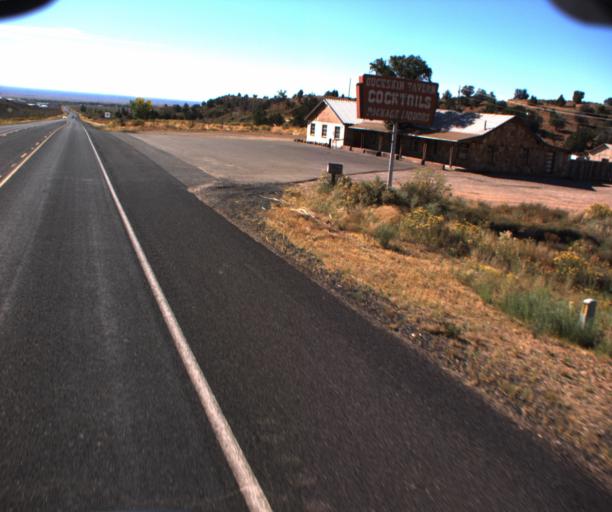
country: US
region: Arizona
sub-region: Coconino County
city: Fredonia
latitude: 36.9893
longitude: -112.5305
